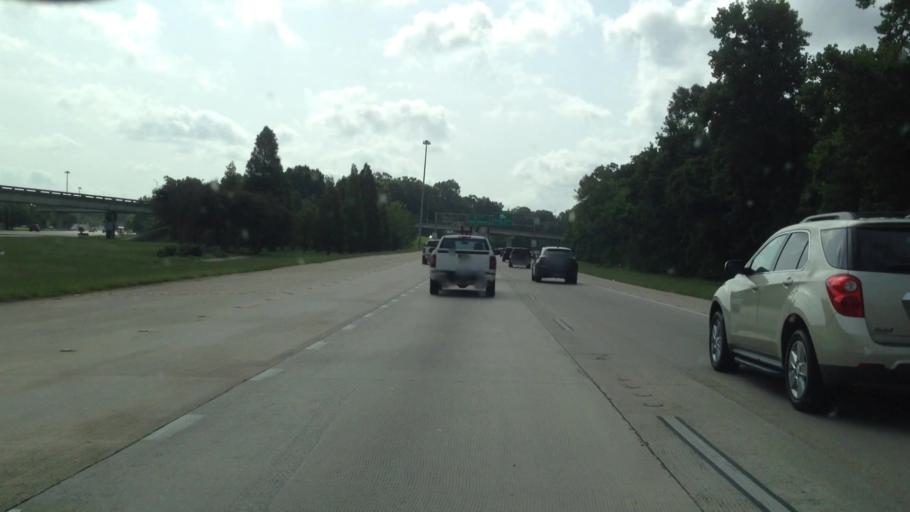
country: US
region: Louisiana
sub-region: East Baton Rouge Parish
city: Westminster
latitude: 30.4179
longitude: -91.1178
